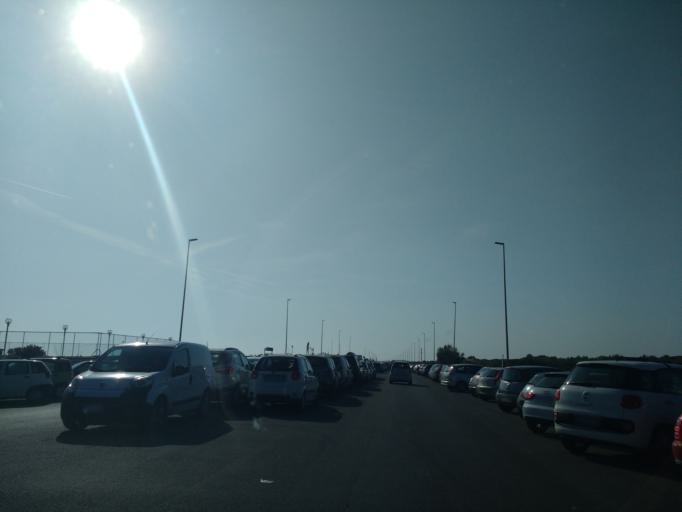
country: IT
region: Latium
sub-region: Citta metropolitana di Roma Capitale
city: Acilia-Castel Fusano-Ostia Antica
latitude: 41.7030
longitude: 12.3435
